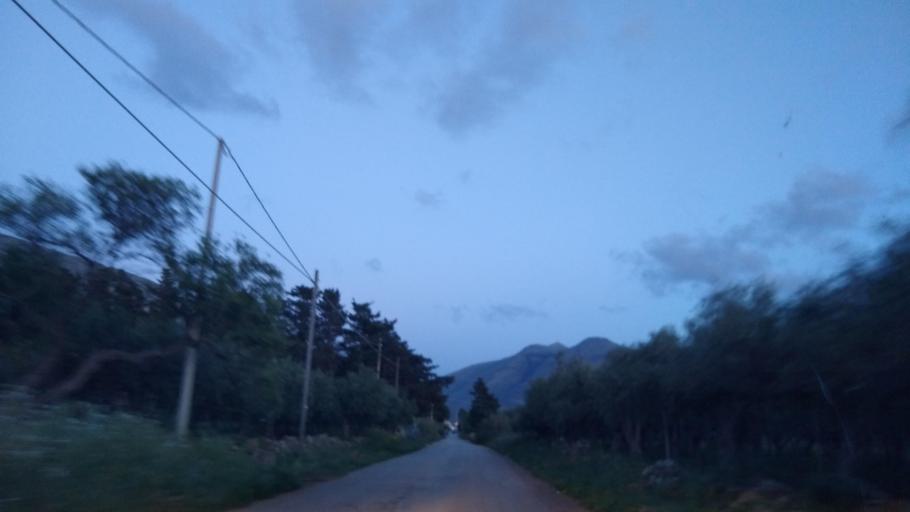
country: IT
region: Sicily
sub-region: Trapani
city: Castelluzzo
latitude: 38.1068
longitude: 12.7290
